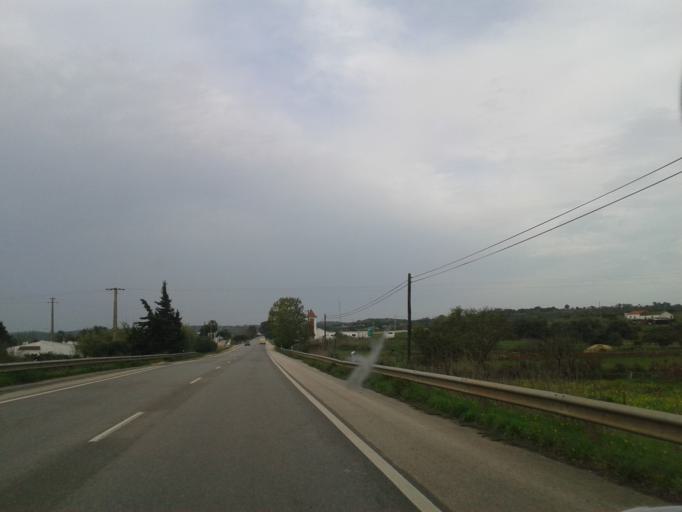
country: PT
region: Faro
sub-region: Lagos
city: Lagos
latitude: 37.0932
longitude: -8.7726
